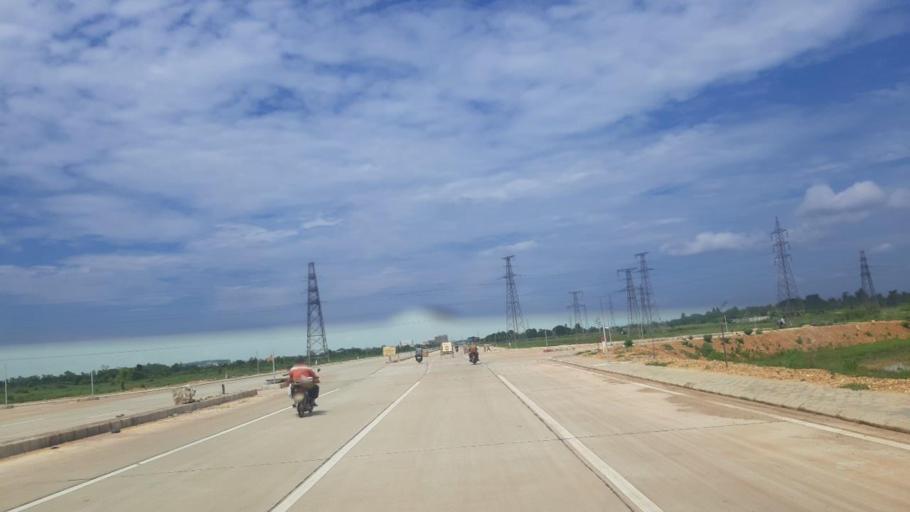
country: LA
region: Vientiane
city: Vientiane
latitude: 18.0251
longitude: 102.6011
